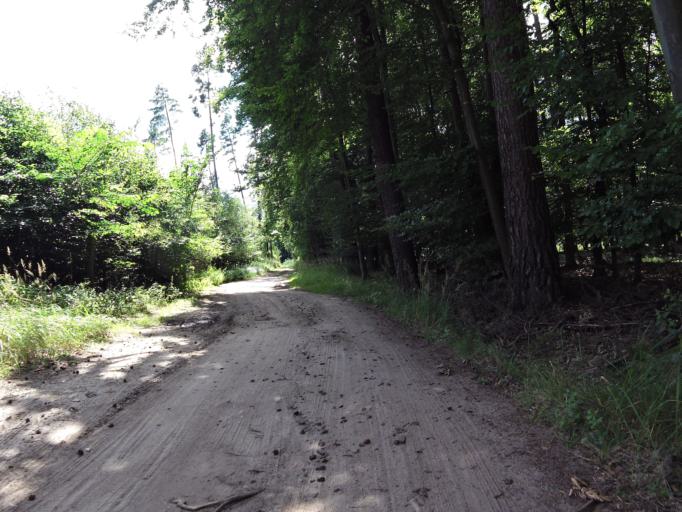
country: DE
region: Brandenburg
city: Lychen
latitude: 53.2601
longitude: 13.4415
